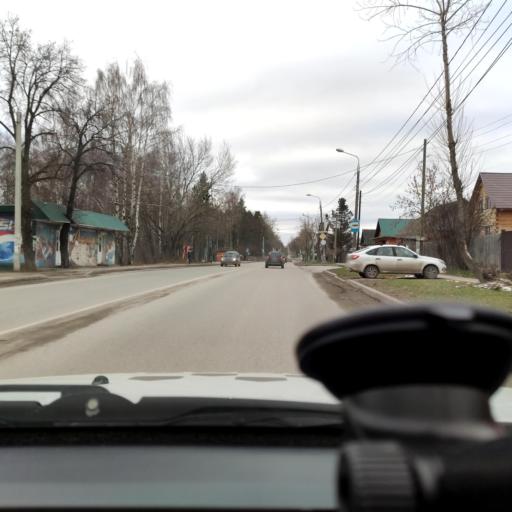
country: RU
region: Perm
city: Perm
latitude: 58.1148
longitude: 56.2967
